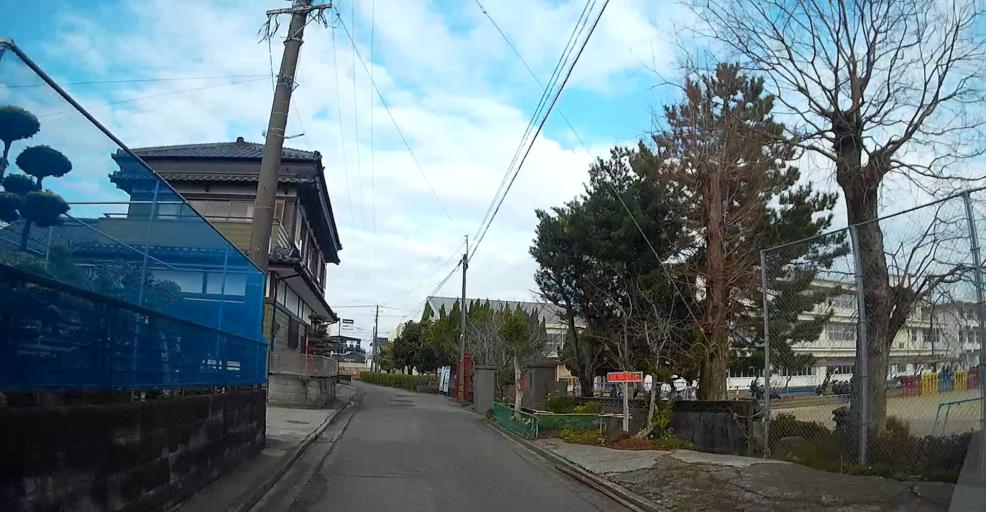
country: JP
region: Kumamoto
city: Hondo
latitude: 32.4624
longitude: 130.1867
